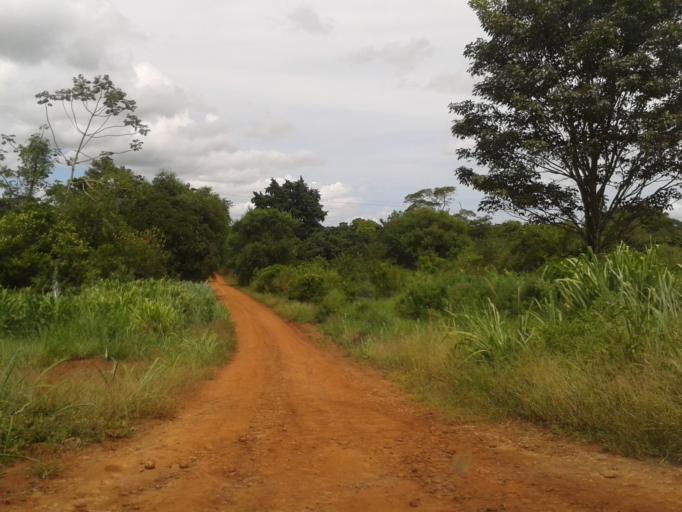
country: BR
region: Minas Gerais
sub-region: Centralina
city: Centralina
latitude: -18.5895
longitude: -49.2707
